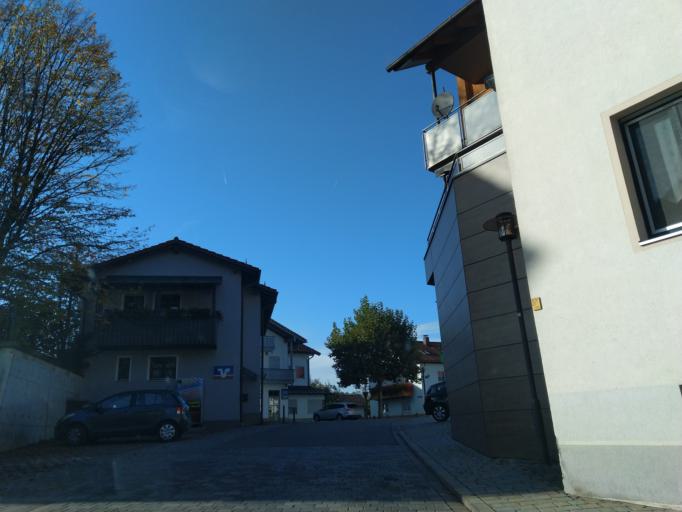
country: DE
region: Bavaria
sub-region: Lower Bavaria
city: Metten
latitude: 48.8616
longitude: 12.8934
